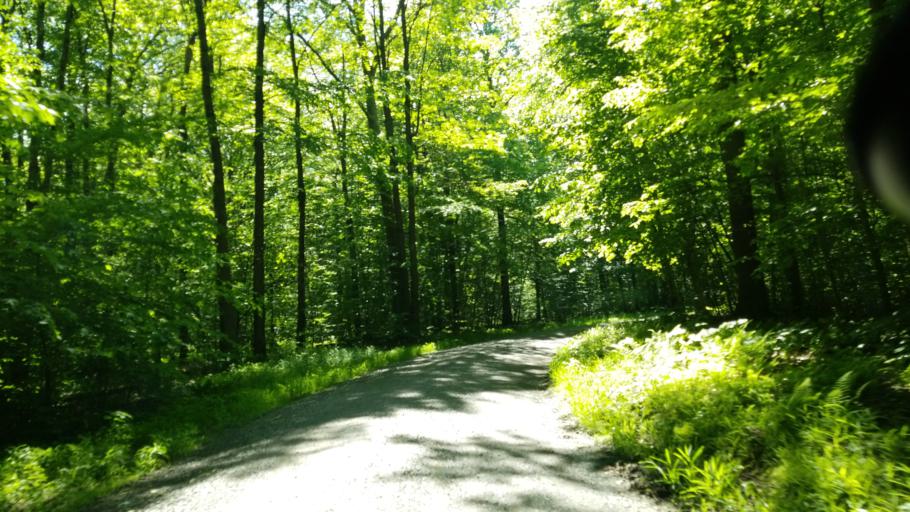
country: US
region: Pennsylvania
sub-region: Clearfield County
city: Clearfield
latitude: 41.2080
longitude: -78.4082
